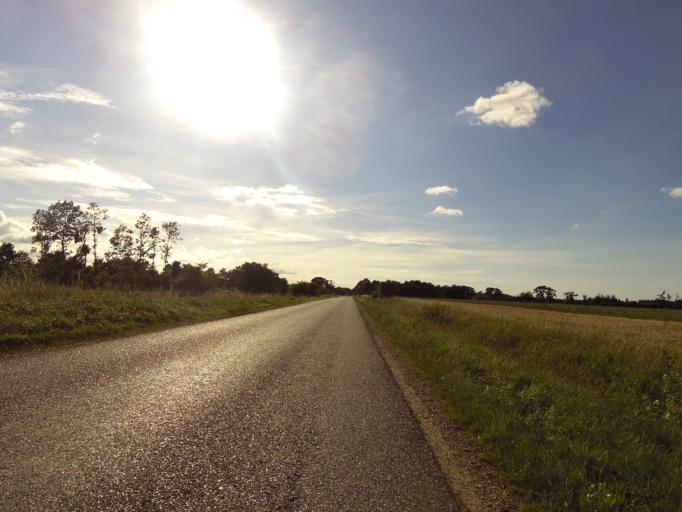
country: DK
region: South Denmark
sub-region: Haderslev Kommune
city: Vojens
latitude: 55.2082
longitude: 9.2582
